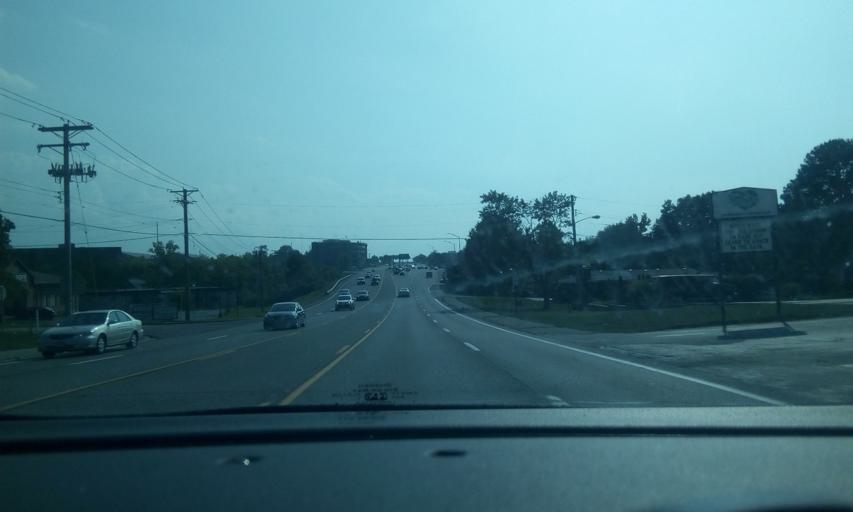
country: US
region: Missouri
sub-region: Saint Louis County
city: Concord
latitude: 38.5161
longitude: -90.3676
